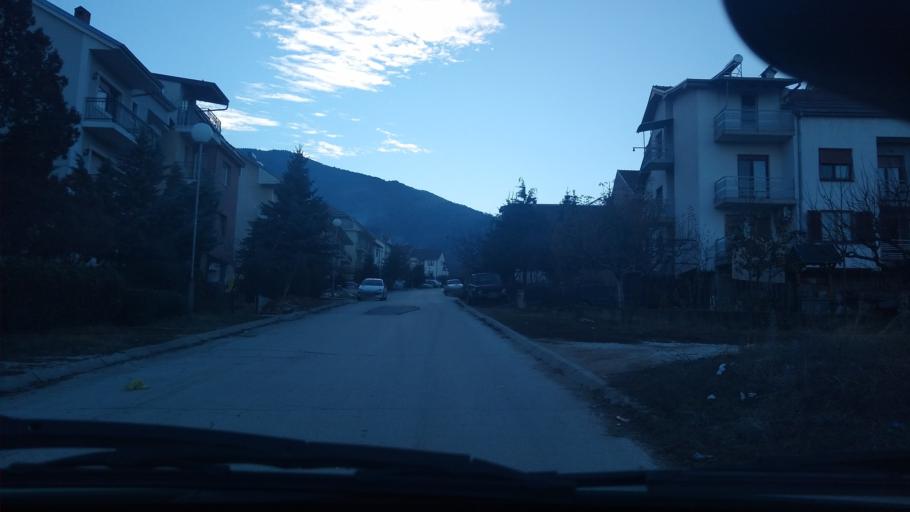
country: MK
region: Bitola
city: Bitola
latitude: 41.0236
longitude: 21.3042
